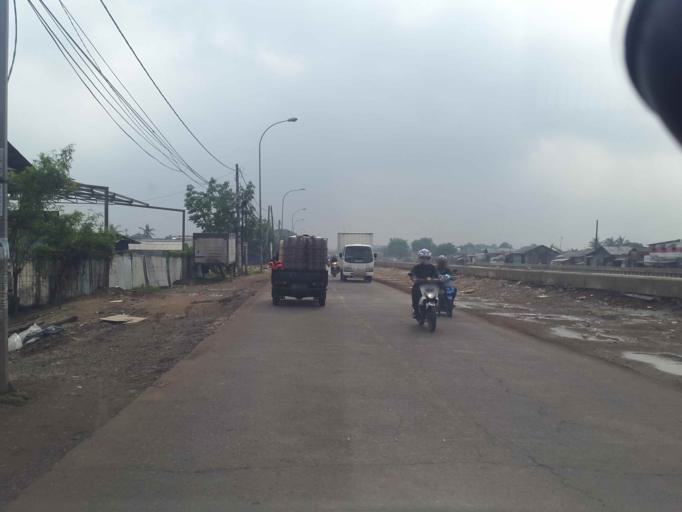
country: ID
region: West Java
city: Cikarang
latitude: -6.2827
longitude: 107.0995
